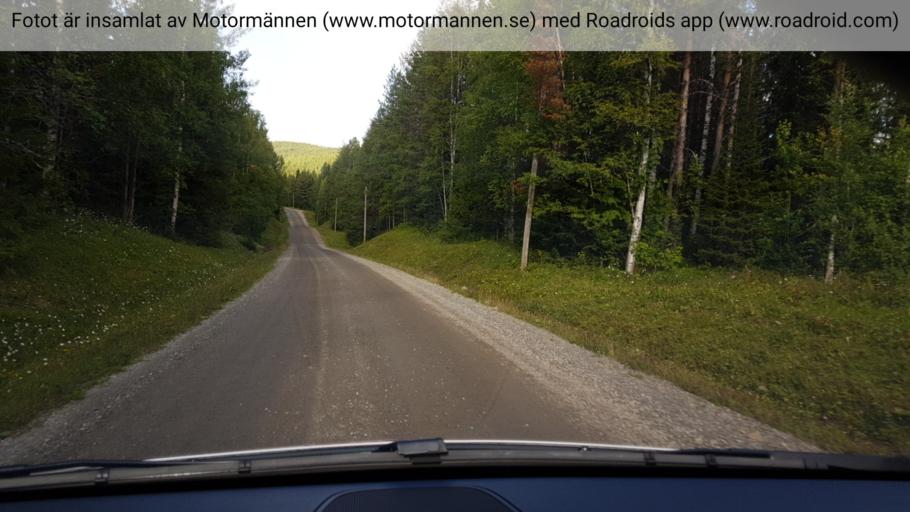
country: SE
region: Jaemtland
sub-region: Ragunda Kommun
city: Hammarstrand
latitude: 63.2841
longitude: 15.9941
